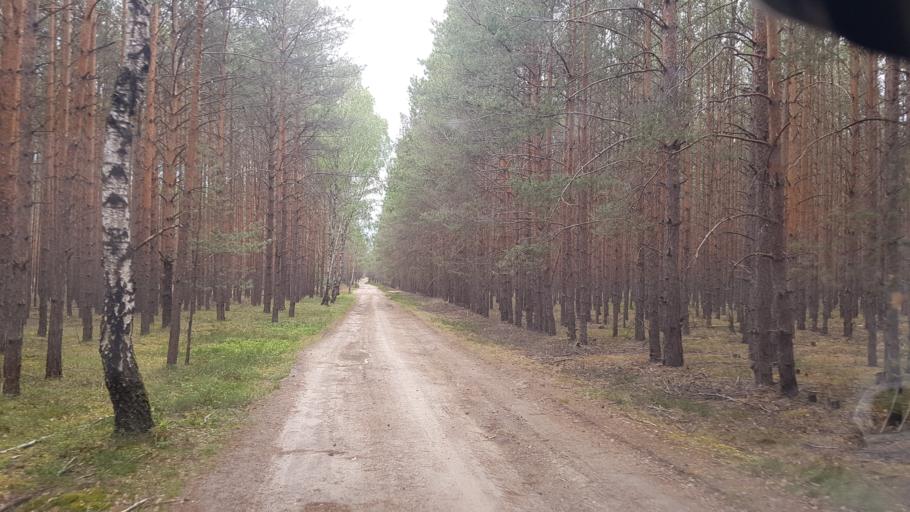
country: DE
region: Brandenburg
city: Finsterwalde
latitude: 51.6242
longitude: 13.6591
